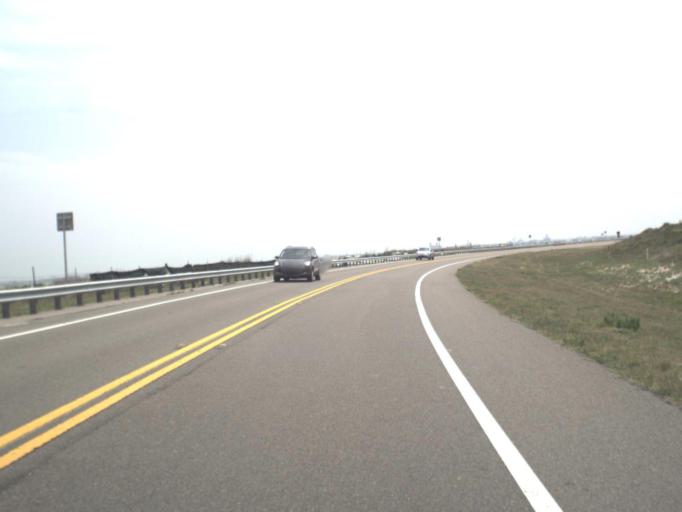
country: US
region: Florida
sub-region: Duval County
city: Atlantic Beach
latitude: 30.4274
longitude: -81.4112
